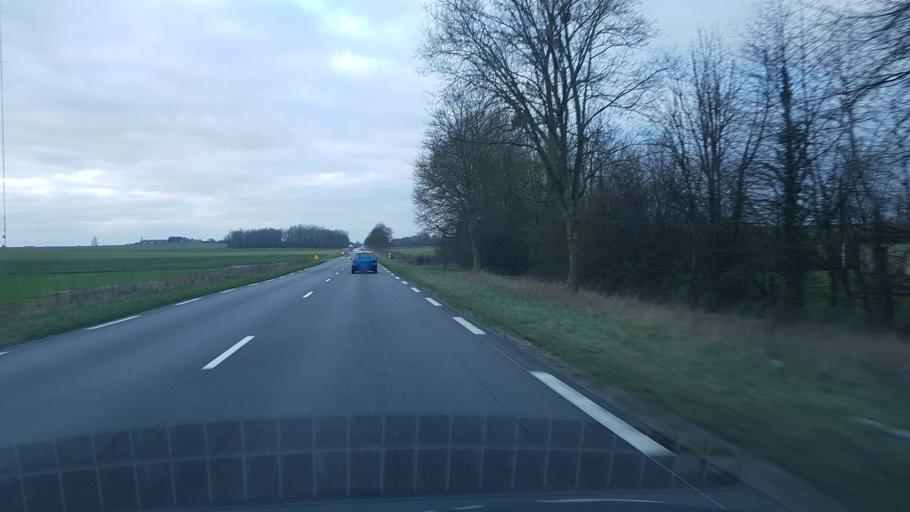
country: FR
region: Champagne-Ardenne
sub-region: Departement de la Marne
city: Esternay
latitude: 48.7172
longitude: 3.5141
